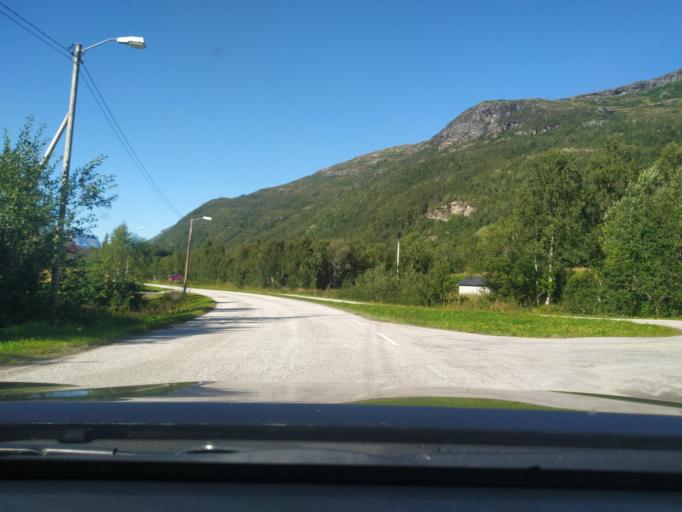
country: NO
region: Troms
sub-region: Salangen
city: Sjovegan
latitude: 68.9390
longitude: 17.7274
